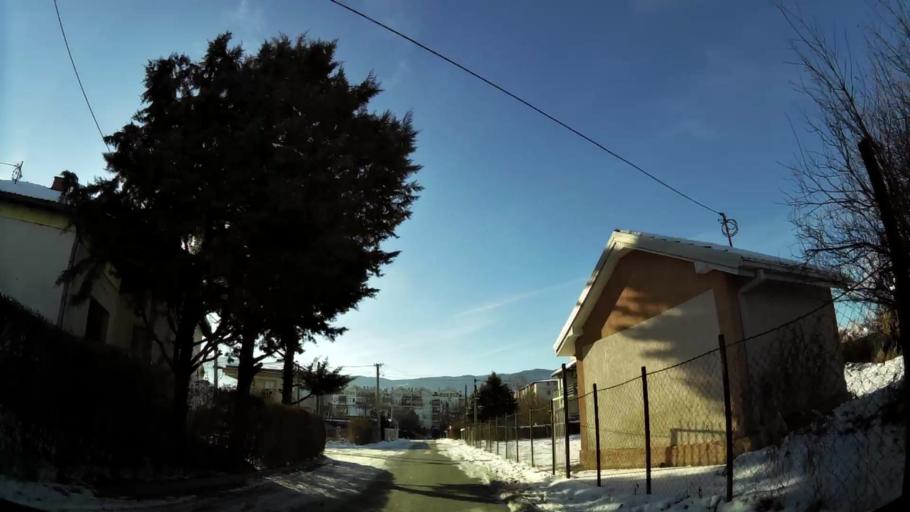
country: MK
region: Saraj
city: Saraj
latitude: 42.0080
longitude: 21.3441
